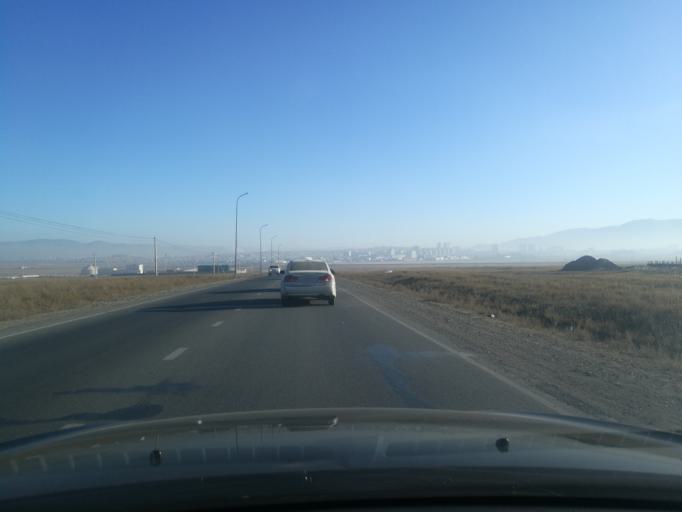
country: MN
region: Ulaanbaatar
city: Ulaanbaatar
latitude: 47.8468
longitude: 106.7338
